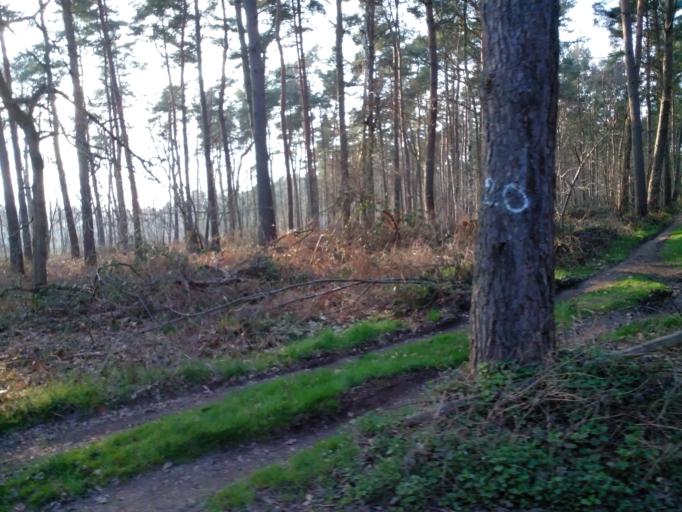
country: BE
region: Flanders
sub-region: Provincie Vlaams-Brabant
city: Oud-Heverlee
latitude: 50.8198
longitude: 4.6868
